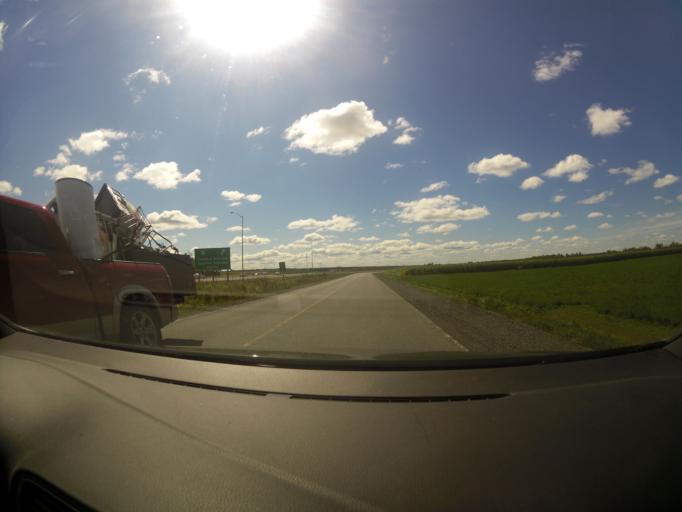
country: CA
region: Ontario
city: Carleton Place
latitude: 45.1539
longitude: -76.0862
